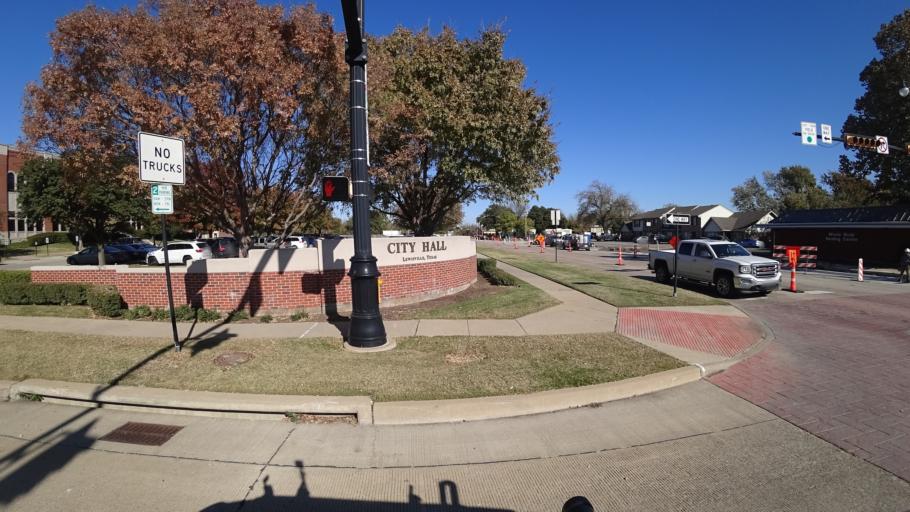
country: US
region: Texas
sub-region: Denton County
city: Lewisville
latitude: 33.0473
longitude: -96.9943
